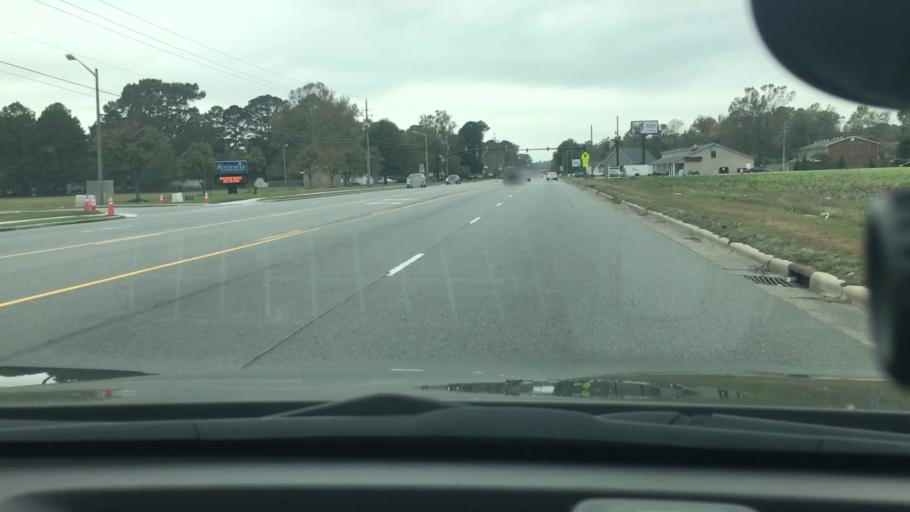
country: US
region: North Carolina
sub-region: Pitt County
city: Summerfield
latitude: 35.5750
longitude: -77.4195
